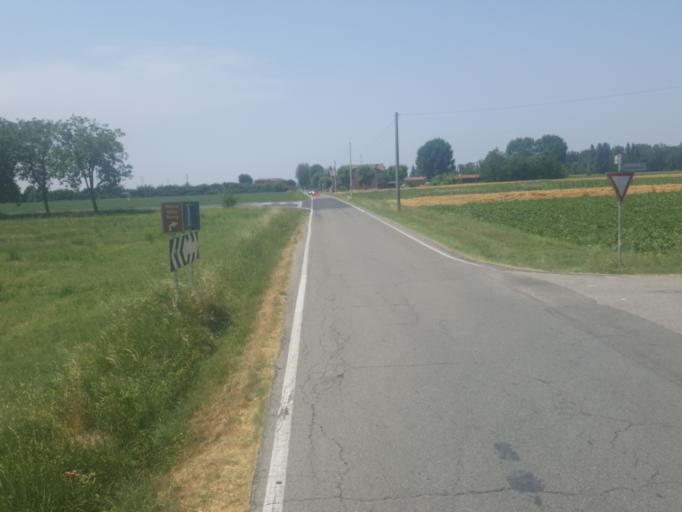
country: IT
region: Emilia-Romagna
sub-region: Provincia di Modena
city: Gaggio
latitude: 44.6241
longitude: 11.0415
